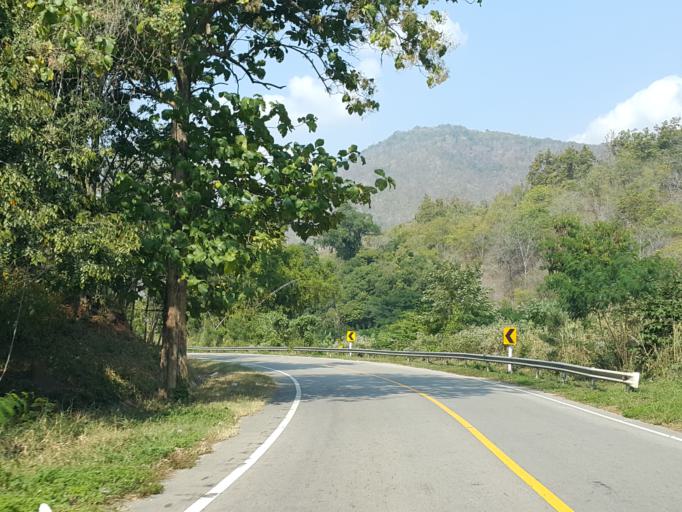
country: TH
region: Chiang Mai
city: Hot
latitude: 18.2206
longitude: 98.5754
